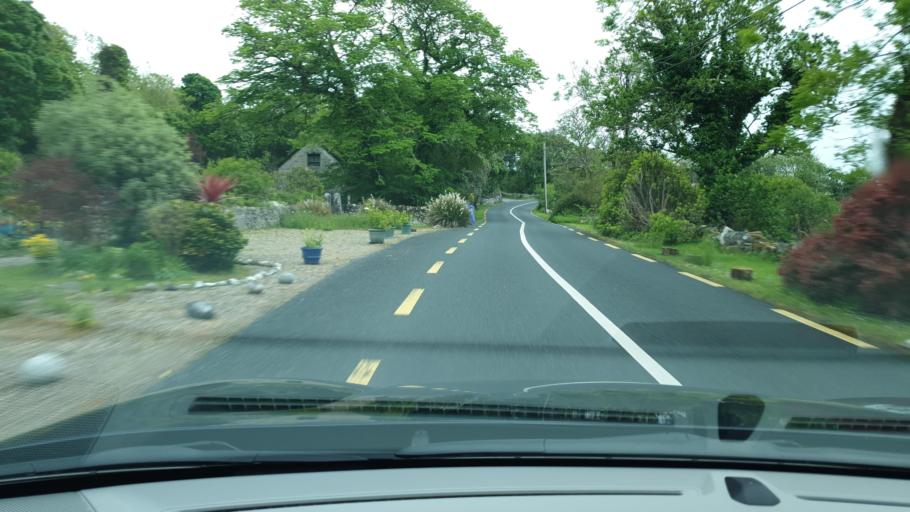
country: IE
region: Connaught
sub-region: County Galway
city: Clifden
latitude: 53.4389
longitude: -9.8683
